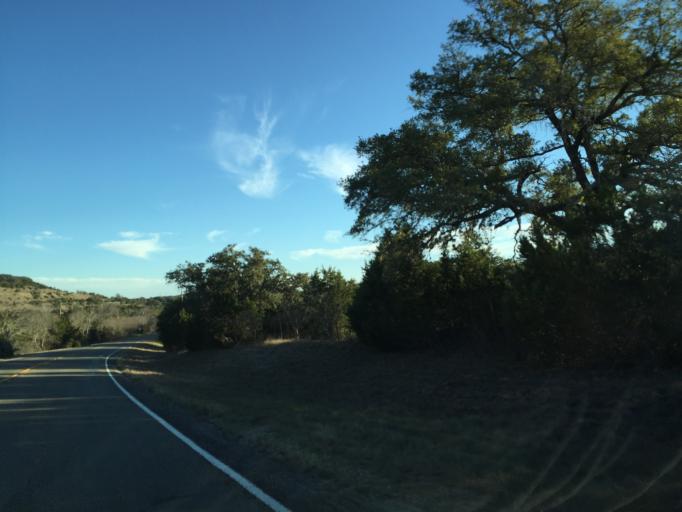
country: US
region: Texas
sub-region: Travis County
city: Lago Vista
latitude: 30.5178
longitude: -98.0434
